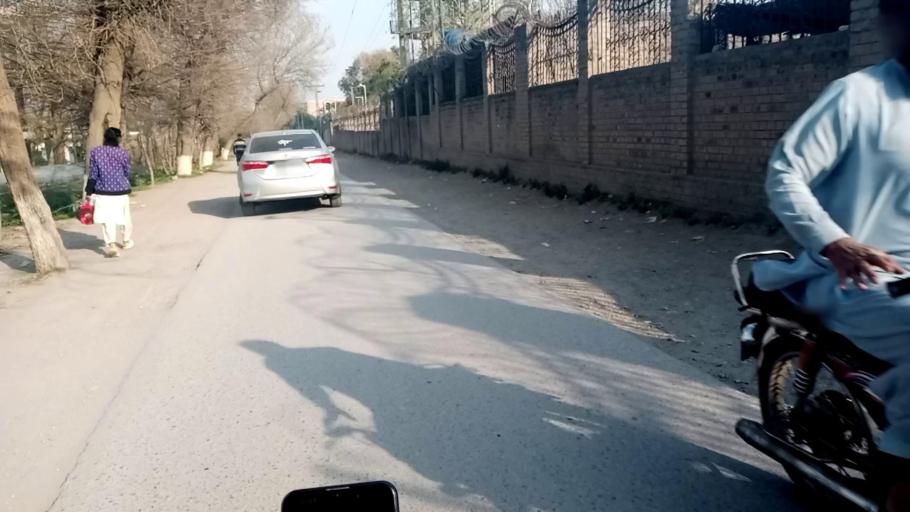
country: PK
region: Khyber Pakhtunkhwa
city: Peshawar
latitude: 34.0056
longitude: 71.4764
